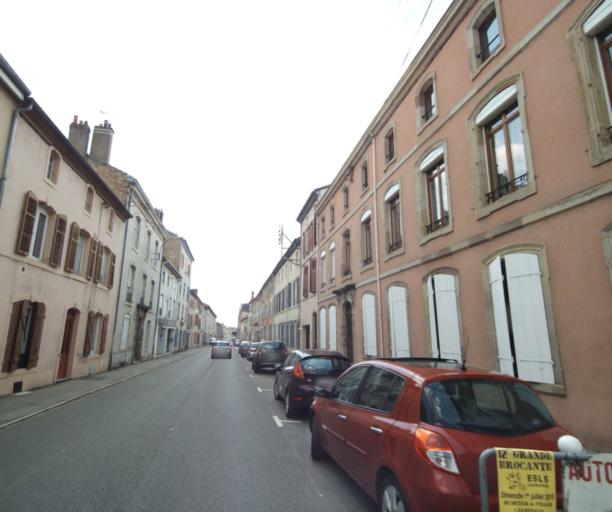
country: FR
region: Lorraine
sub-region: Departement de Meurthe-et-Moselle
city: Luneville
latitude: 48.5896
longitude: 6.4900
